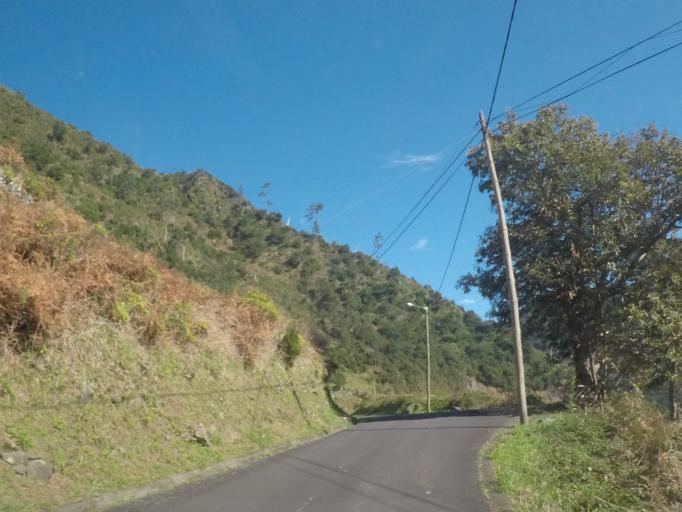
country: PT
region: Madeira
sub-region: Camara de Lobos
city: Curral das Freiras
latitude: 32.7834
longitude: -16.9781
